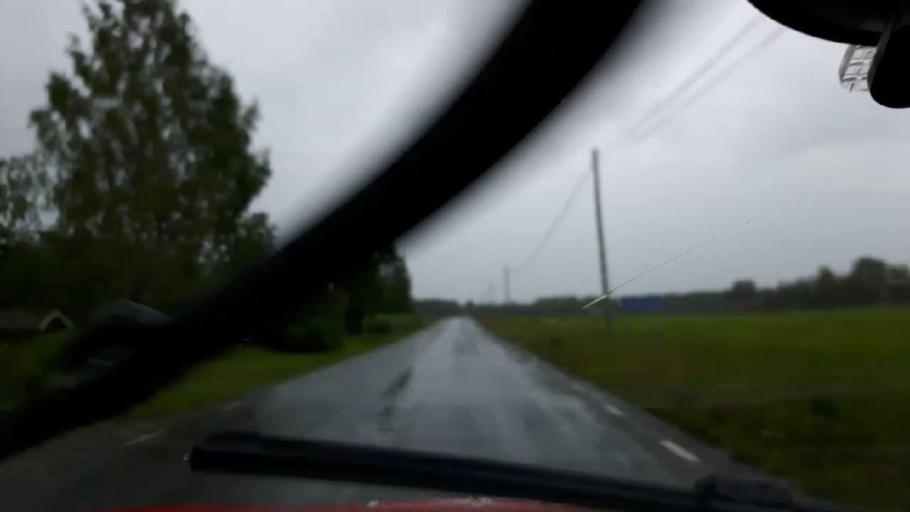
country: SE
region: Jaemtland
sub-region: OEstersunds Kommun
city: Brunflo
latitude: 62.9939
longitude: 14.7868
